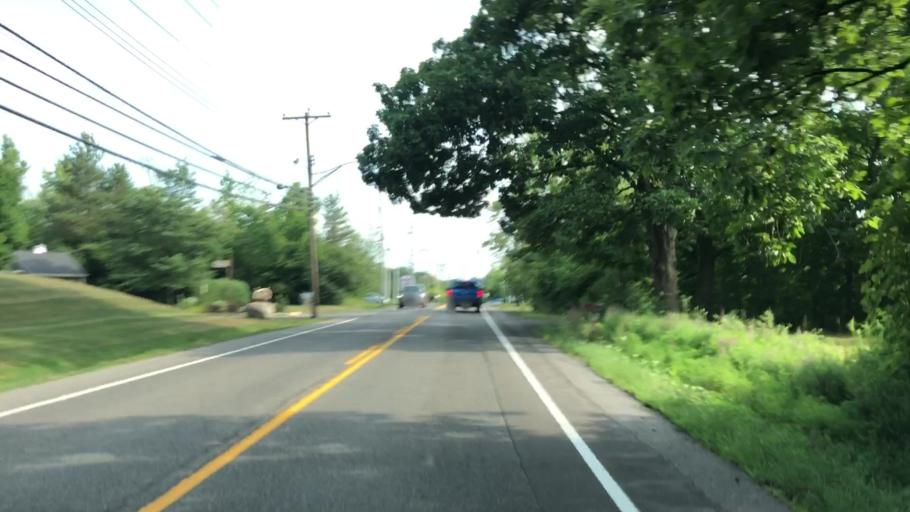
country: US
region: New York
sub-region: Erie County
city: Elma Center
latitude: 42.8367
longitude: -78.6369
